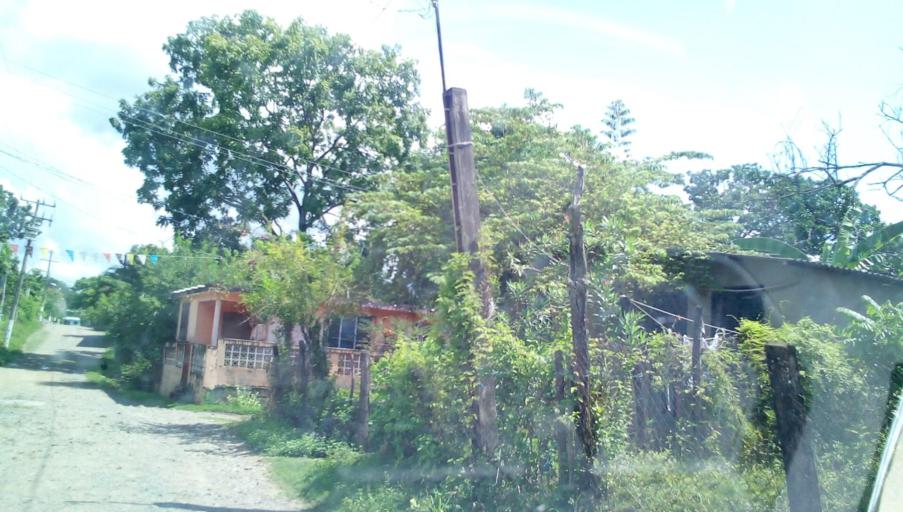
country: MX
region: Veracruz
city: Tamalin
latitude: 21.3670
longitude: -97.8006
